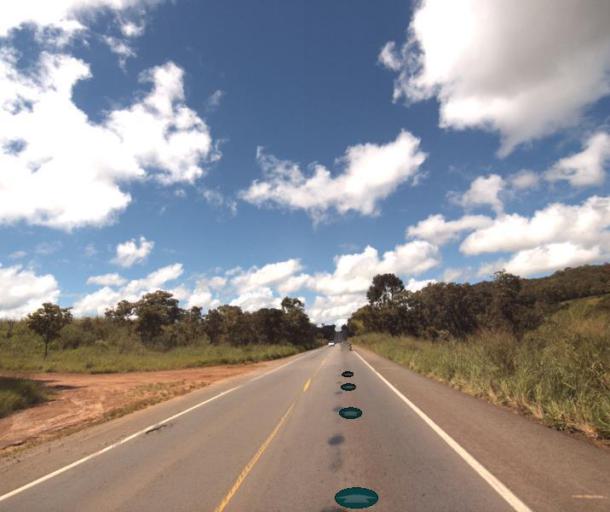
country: BR
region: Goias
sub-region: Jaragua
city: Jaragua
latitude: -15.8782
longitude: -49.2482
